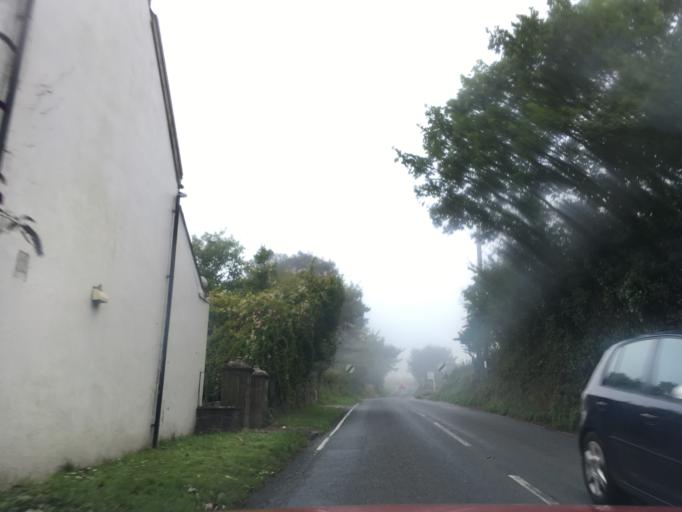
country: GB
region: Wales
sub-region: Pembrokeshire
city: Saint David's
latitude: 51.8797
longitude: -5.2176
